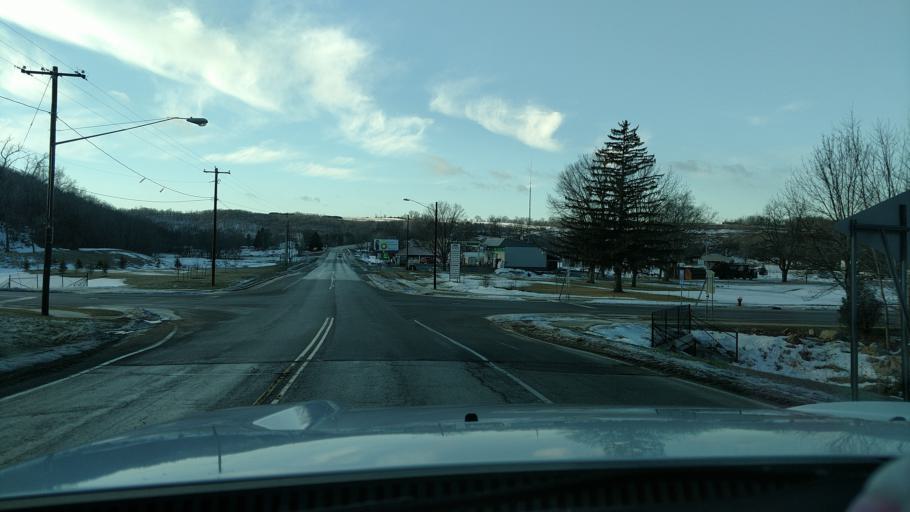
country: US
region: Minnesota
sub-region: Olmsted County
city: Oronoco
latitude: 44.2836
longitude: -92.4221
